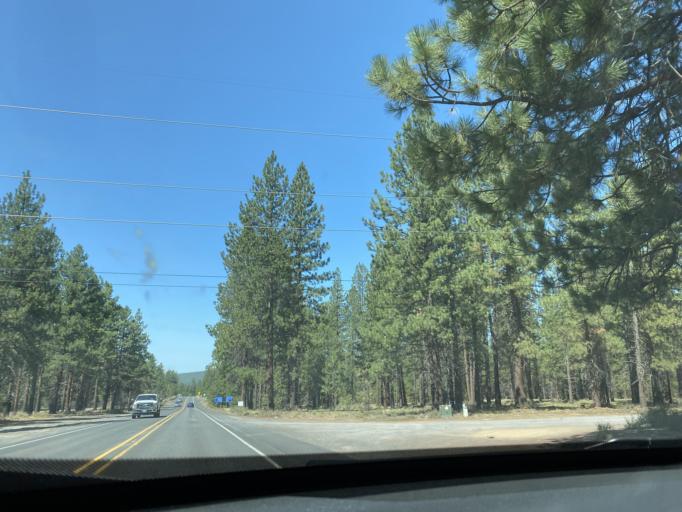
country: US
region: Oregon
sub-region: Deschutes County
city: Sunriver
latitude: 43.8695
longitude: -121.4252
